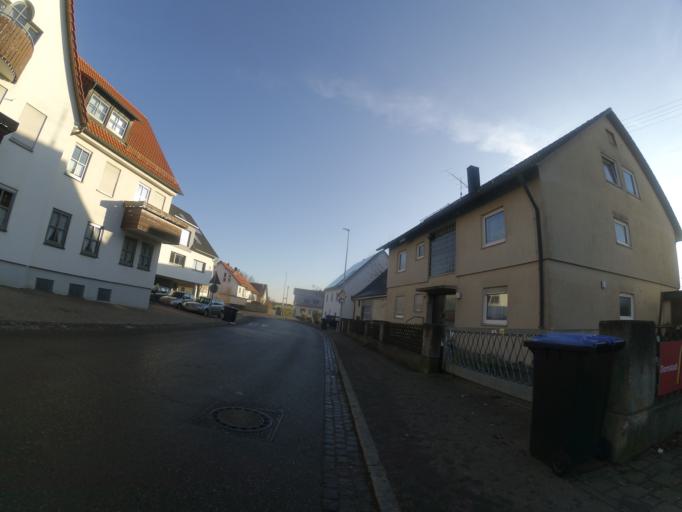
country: DE
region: Baden-Wuerttemberg
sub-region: Tuebingen Region
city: Dornstadt
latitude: 48.4551
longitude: 9.9095
